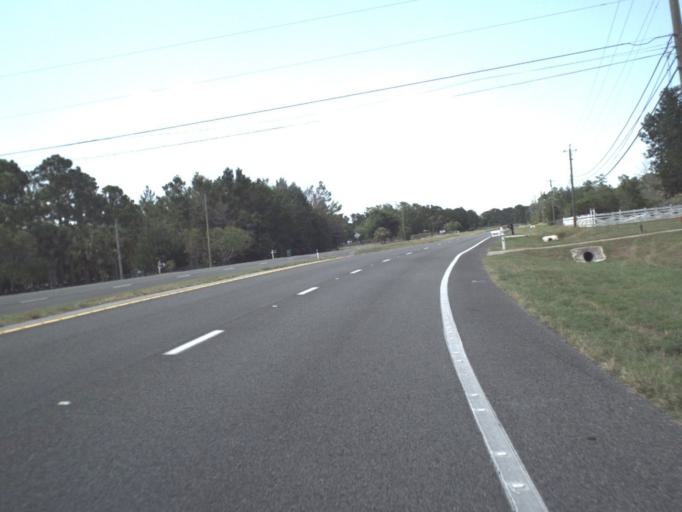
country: US
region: Florida
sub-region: Brevard County
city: Mims
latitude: 28.7367
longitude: -80.8682
